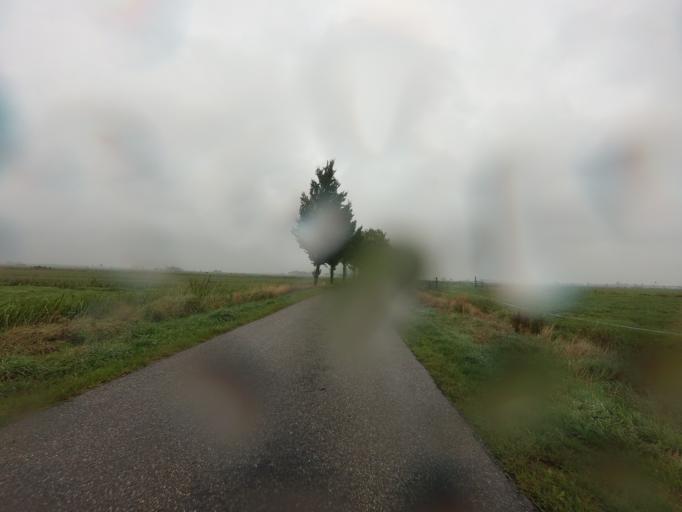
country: NL
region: Friesland
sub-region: Gemeente Boarnsterhim
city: Aldeboarn
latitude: 53.0647
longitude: 5.9179
